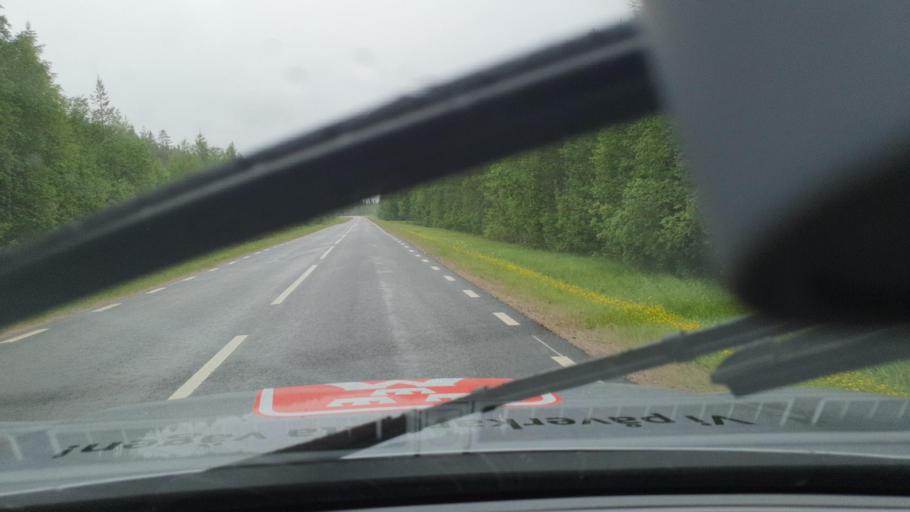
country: SE
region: Norrbotten
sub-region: Overtornea Kommun
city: OEvertornea
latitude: 66.4449
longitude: 23.3102
